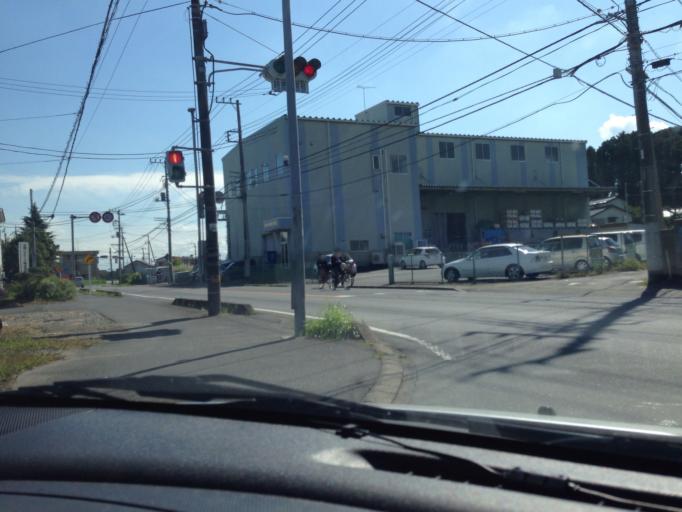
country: JP
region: Ibaraki
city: Ami
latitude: 36.0657
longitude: 140.2105
